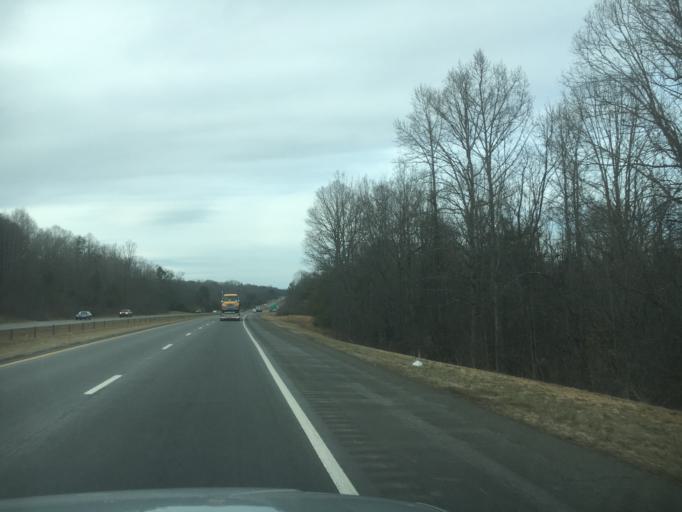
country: US
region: North Carolina
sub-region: Catawba County
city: Mountain View
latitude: 35.6624
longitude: -81.3239
